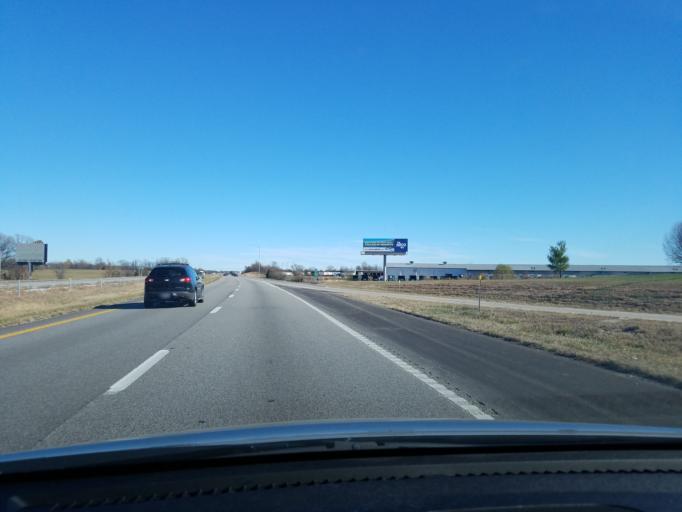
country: US
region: Missouri
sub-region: Greene County
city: Strafford
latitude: 37.2510
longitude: -93.1806
